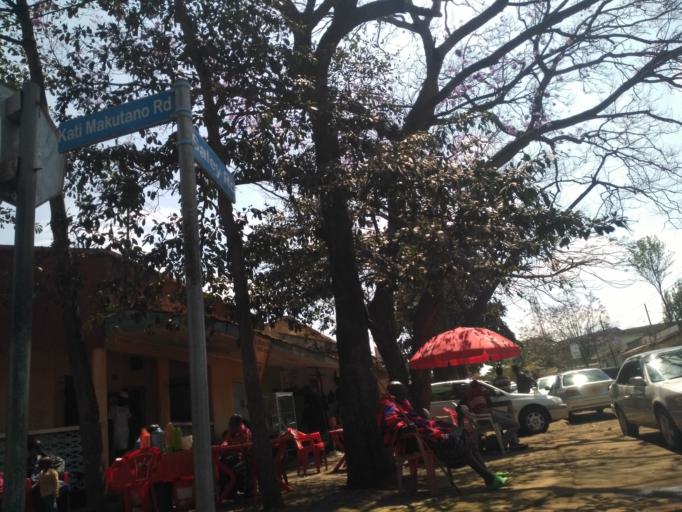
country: TZ
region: Arusha
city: Arusha
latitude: -3.3703
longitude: 36.6802
